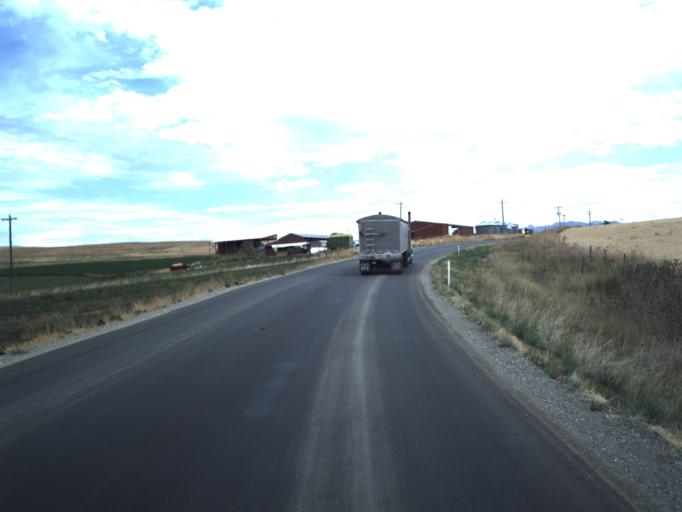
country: US
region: Utah
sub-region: Cache County
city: Benson
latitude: 41.8622
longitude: -111.9753
